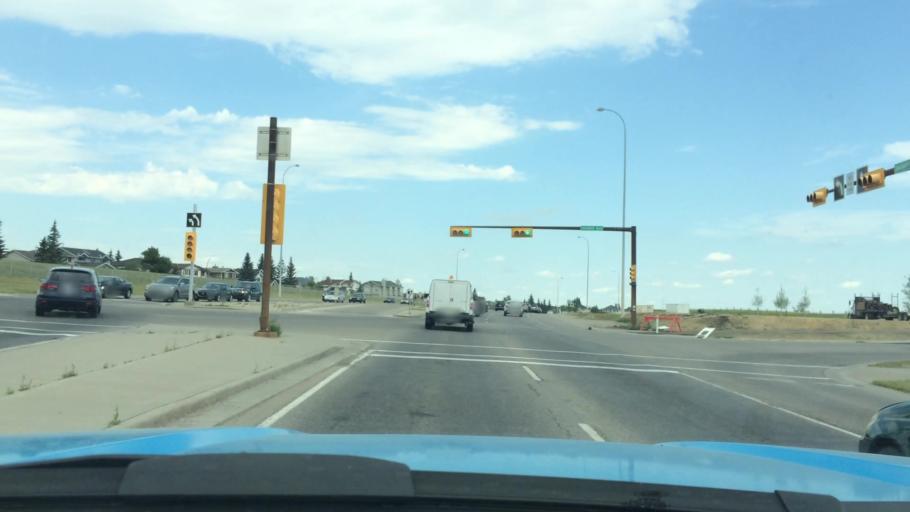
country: CA
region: Alberta
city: Calgary
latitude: 51.1265
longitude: -114.1332
